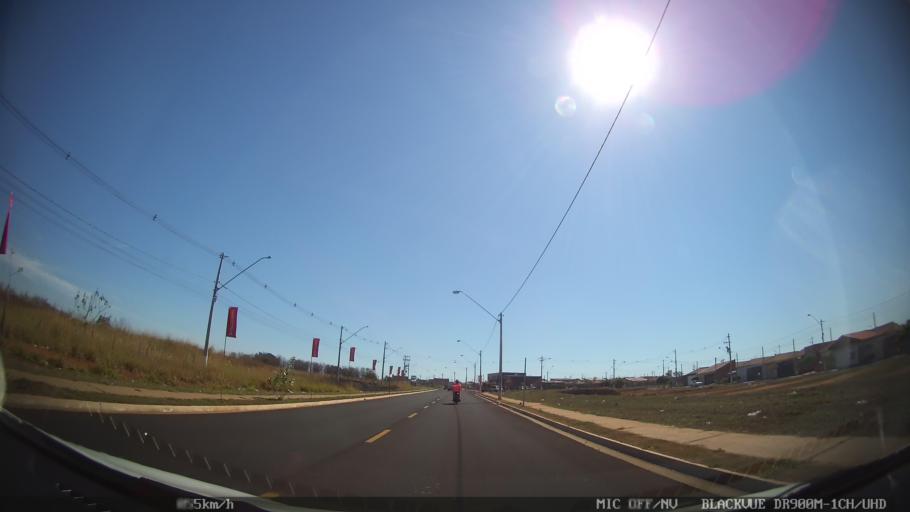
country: BR
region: Sao Paulo
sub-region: Sao Jose Do Rio Preto
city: Sao Jose do Rio Preto
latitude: -20.7563
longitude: -49.4375
